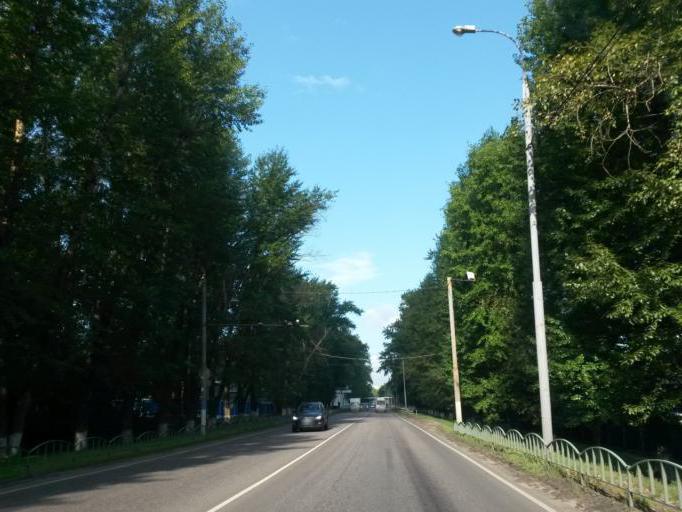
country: RU
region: Moskovskaya
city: Alekseyevka
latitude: 55.6412
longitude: 37.8092
